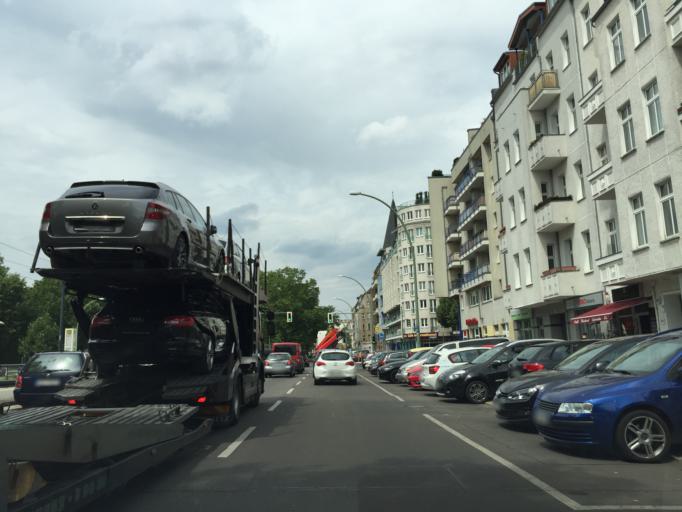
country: DE
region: Berlin
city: Friedrichshain Bezirk
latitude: 52.5290
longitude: 13.4452
